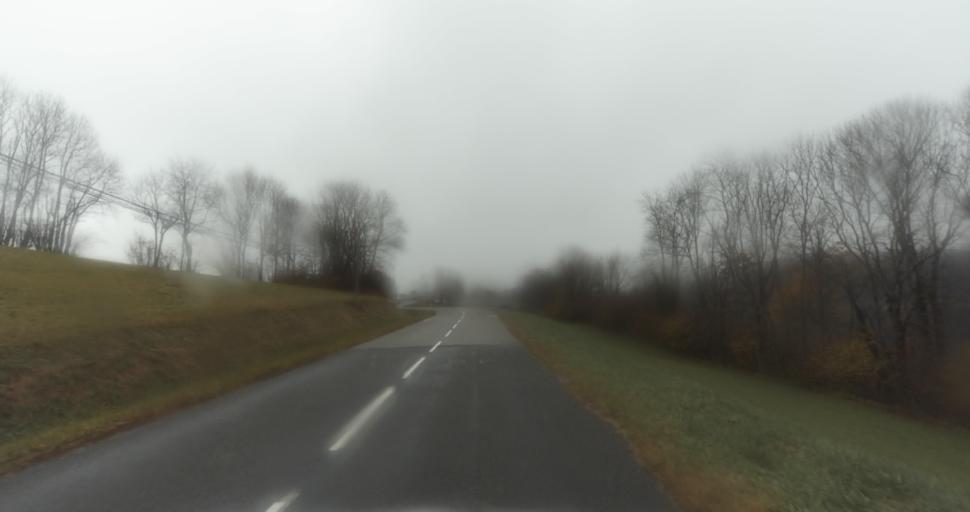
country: FR
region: Rhone-Alpes
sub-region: Departement de la Haute-Savoie
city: Etaux
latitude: 46.0240
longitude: 6.2861
